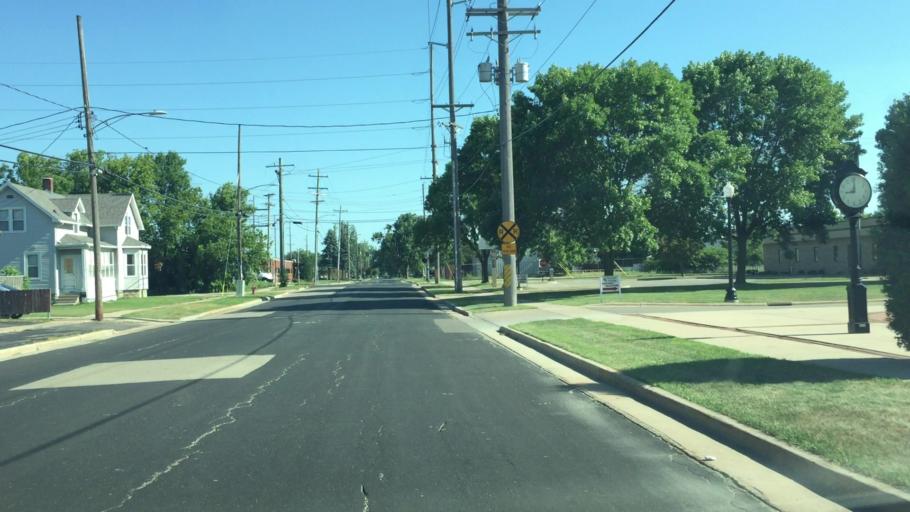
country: US
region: Wisconsin
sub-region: Winnebago County
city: Menasha
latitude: 44.2053
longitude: -88.4491
